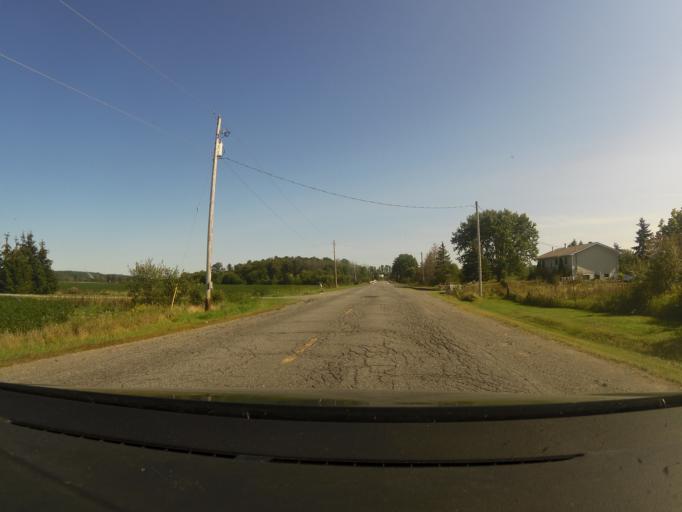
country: CA
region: Ontario
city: Carleton Place
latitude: 45.3696
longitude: -76.1132
